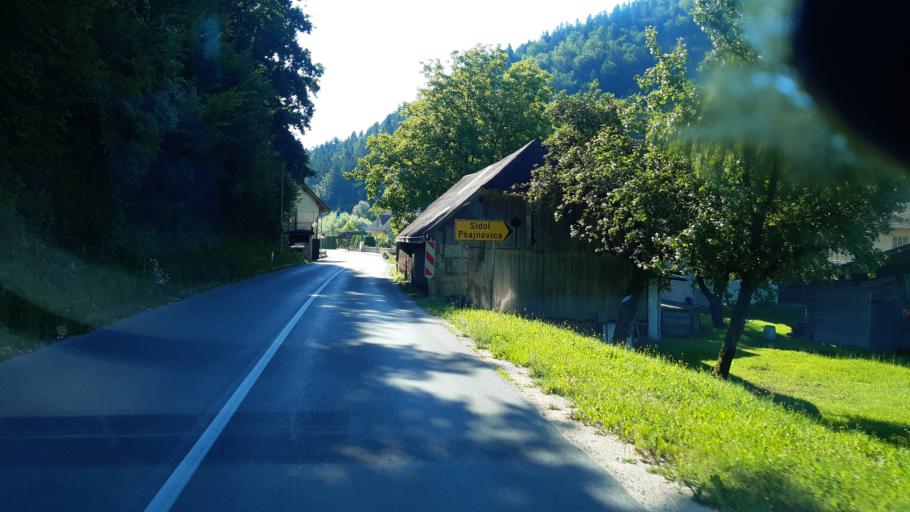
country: SI
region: Lukovica
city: Lukovica pri Domzalah
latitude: 46.2150
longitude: 14.7299
